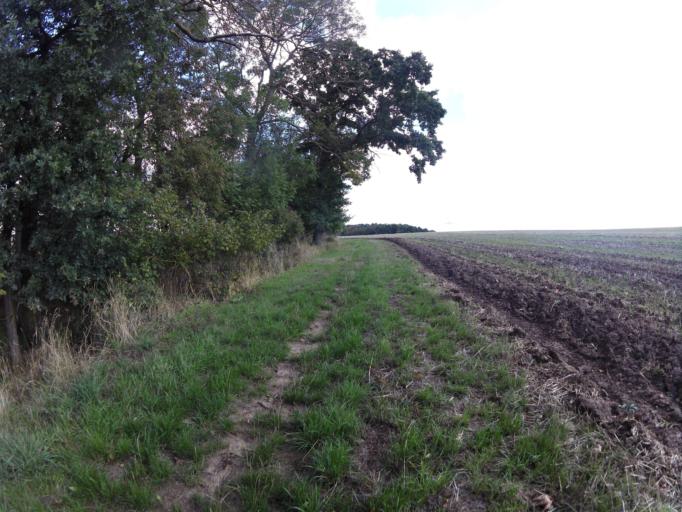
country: DE
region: Bavaria
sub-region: Regierungsbezirk Unterfranken
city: Frickenhausen
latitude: 49.6941
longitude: 10.0917
